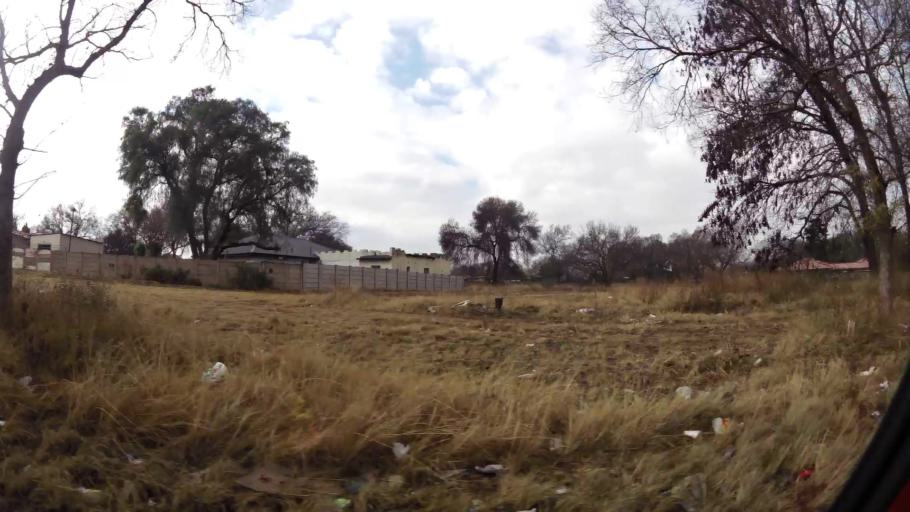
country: ZA
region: Gauteng
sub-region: Sedibeng District Municipality
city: Vanderbijlpark
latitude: -26.6931
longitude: 27.8121
